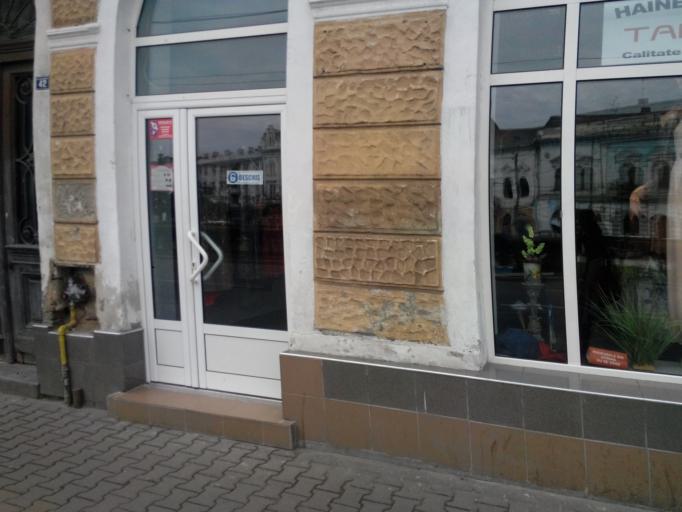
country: RO
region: Cluj
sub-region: Municipiul Cluj-Napoca
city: Cluj-Napoca
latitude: 46.7739
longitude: 23.5889
